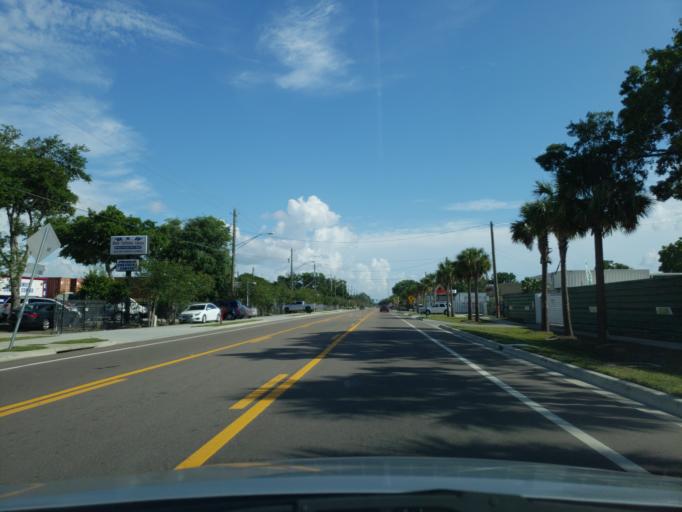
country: US
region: Florida
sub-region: Hillsborough County
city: Egypt Lake-Leto
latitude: 27.9858
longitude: -82.5136
